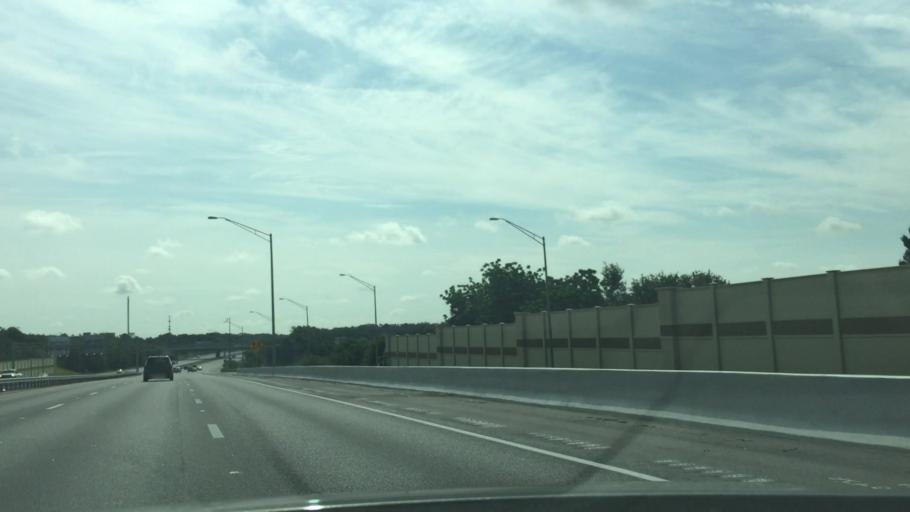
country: US
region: Florida
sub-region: Orange County
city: Orlovista
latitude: 28.5479
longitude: -81.4904
